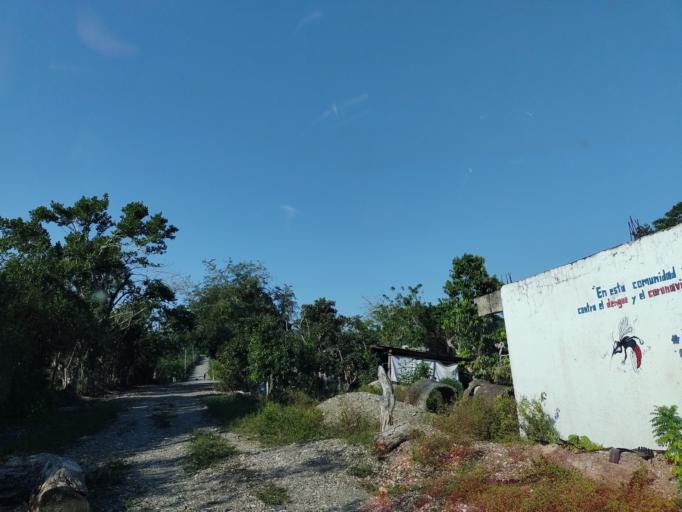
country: MX
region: Veracruz
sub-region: Papantla
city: Polutla
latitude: 20.4556
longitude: -97.2268
